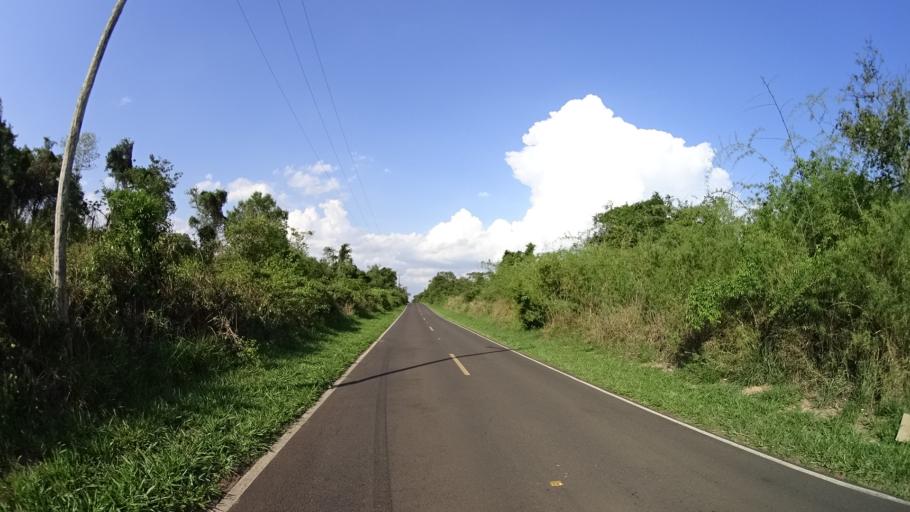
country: BR
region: Sao Paulo
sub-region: Urupes
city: Urupes
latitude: -21.3786
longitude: -49.4843
